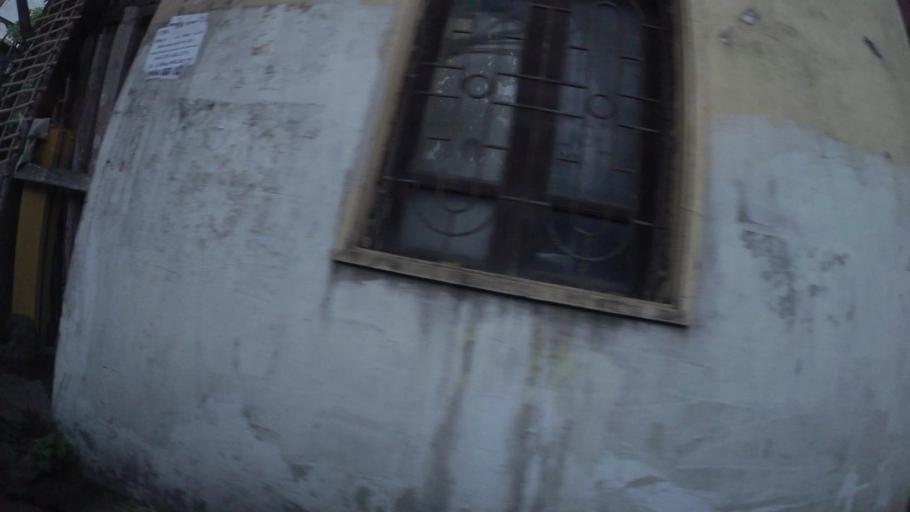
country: VN
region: Ha Noi
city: Hai BaTrung
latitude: 21.0137
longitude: 105.8634
